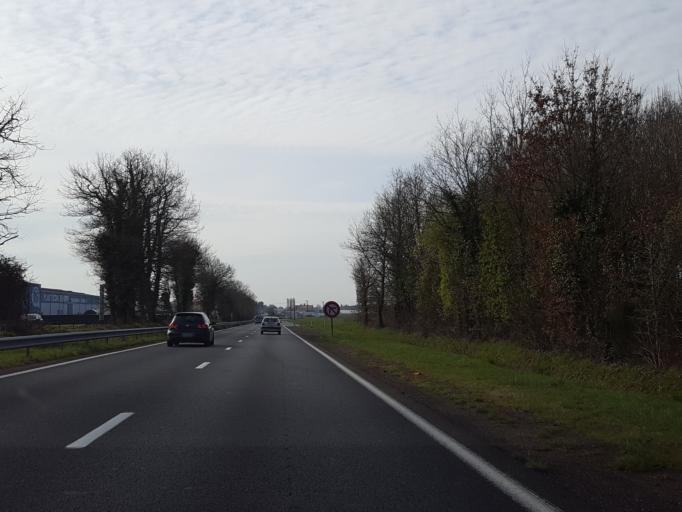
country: FR
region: Pays de la Loire
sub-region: Departement de la Vendee
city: Mouilleron-le-Captif
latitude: 46.7442
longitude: -1.4306
